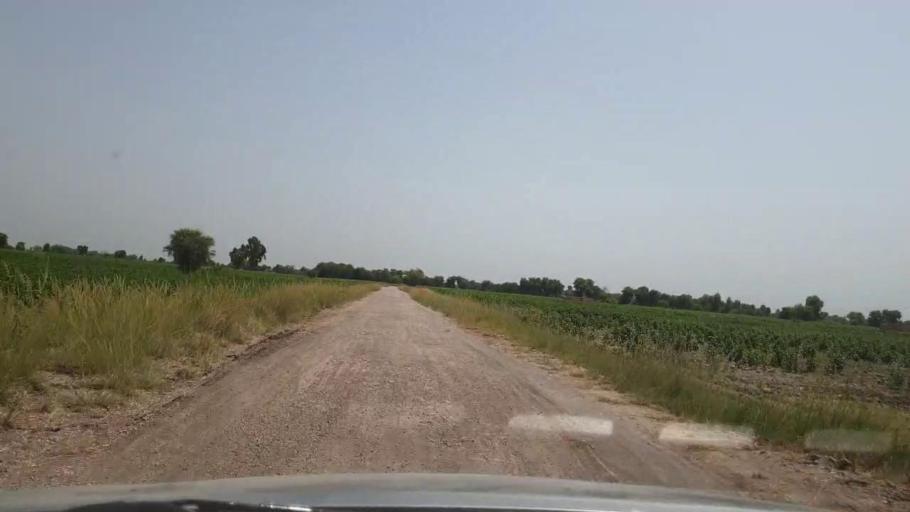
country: PK
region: Sindh
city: Pano Aqil
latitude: 27.8009
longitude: 69.2419
